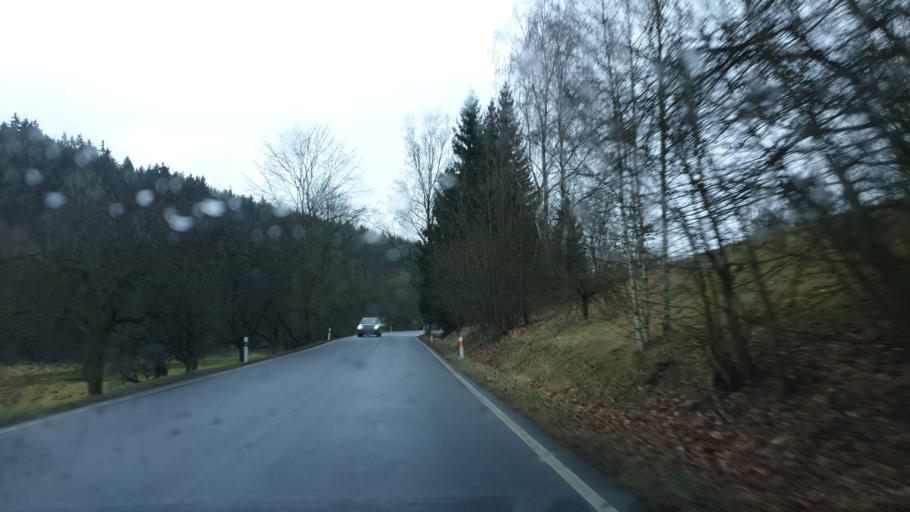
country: CZ
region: Karlovarsky
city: As
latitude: 50.2422
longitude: 12.1905
